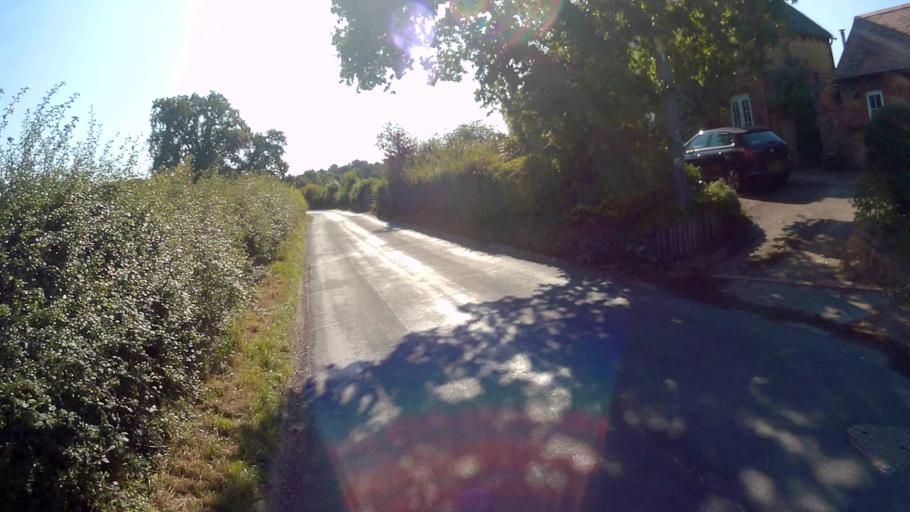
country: GB
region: England
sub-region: Surrey
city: Churt
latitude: 51.1614
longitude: -0.8071
